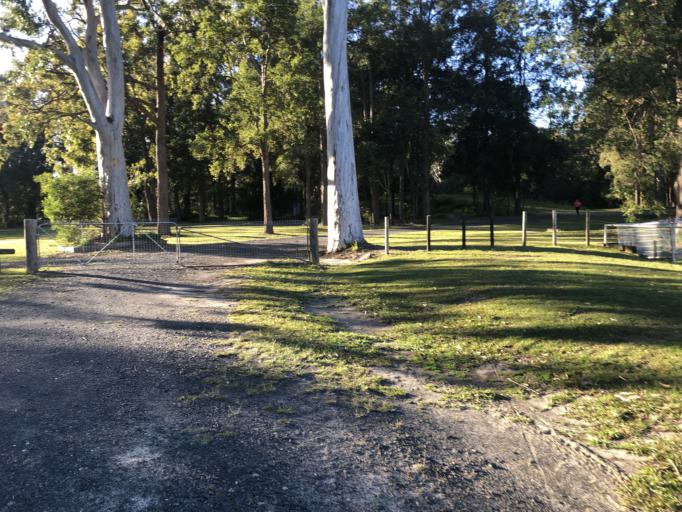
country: AU
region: New South Wales
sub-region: Coffs Harbour
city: Coffs Harbour
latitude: -30.2926
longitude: 153.1219
